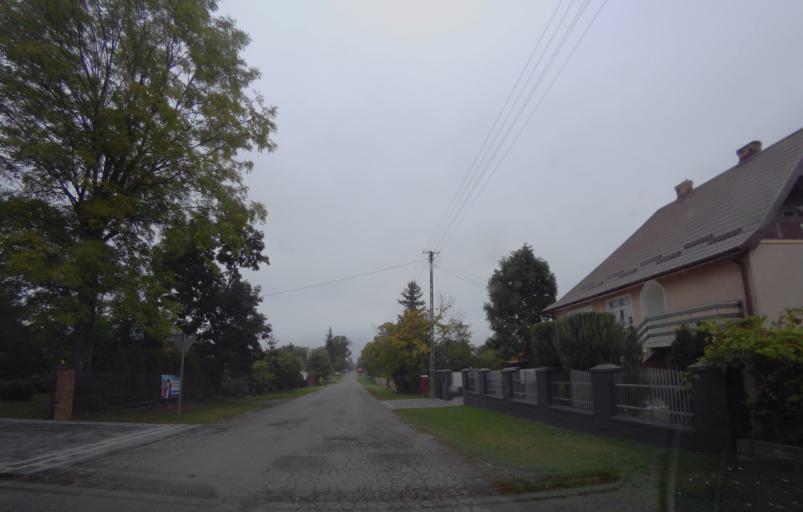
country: PL
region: Lublin Voivodeship
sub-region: Powiat chelmski
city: Sawin
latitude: 51.2143
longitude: 23.4534
